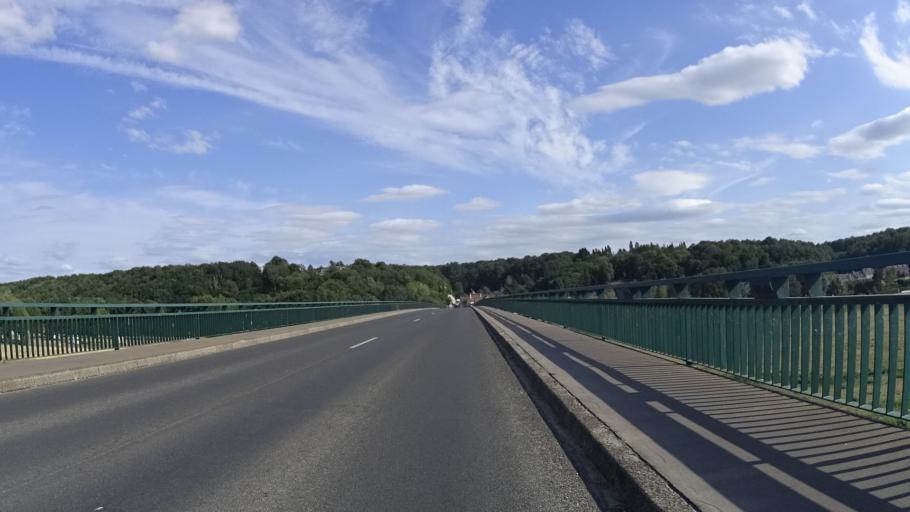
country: FR
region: Centre
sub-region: Departement du Loir-et-Cher
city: Chaumont-sur-Loire
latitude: 47.4853
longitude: 1.1907
